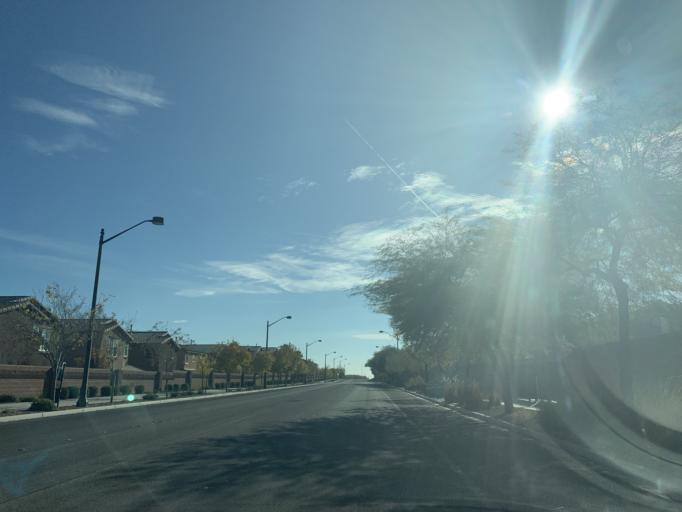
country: US
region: Nevada
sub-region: Clark County
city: Summerlin South
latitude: 36.3094
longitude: -115.3014
